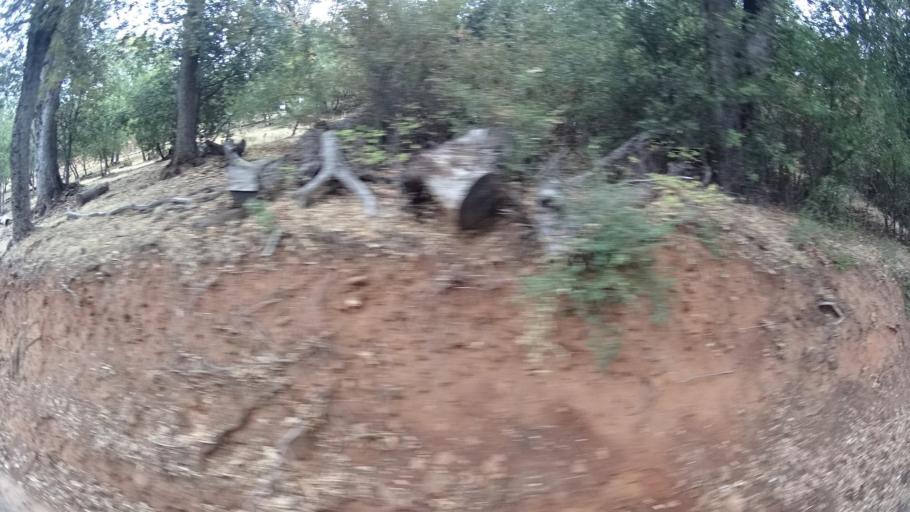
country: US
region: California
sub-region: San Diego County
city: Julian
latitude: 33.0101
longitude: -116.6116
